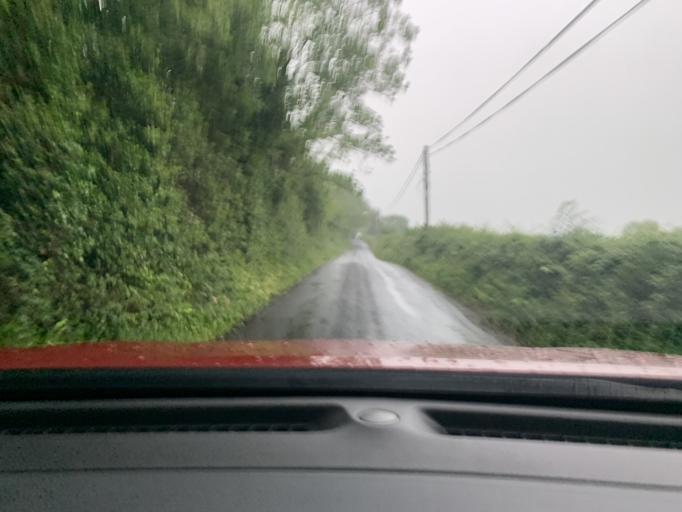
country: IE
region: Connaught
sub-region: Sligo
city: Sligo
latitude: 54.3301
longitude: -8.4172
